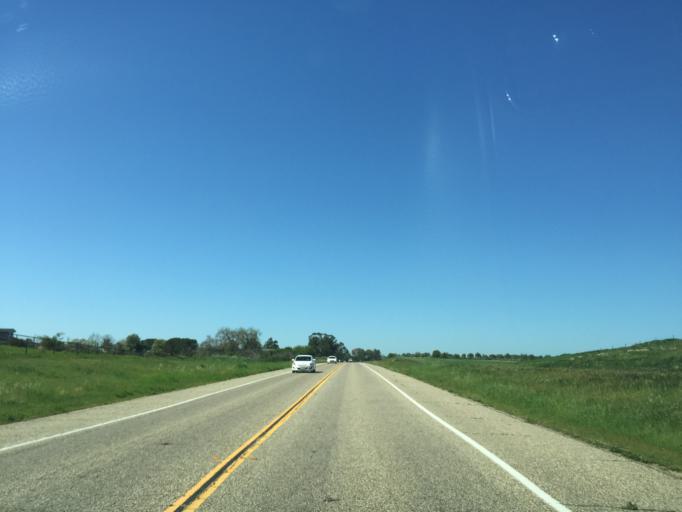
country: US
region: California
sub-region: Santa Barbara County
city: Santa Ynez
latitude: 34.6249
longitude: -120.0722
